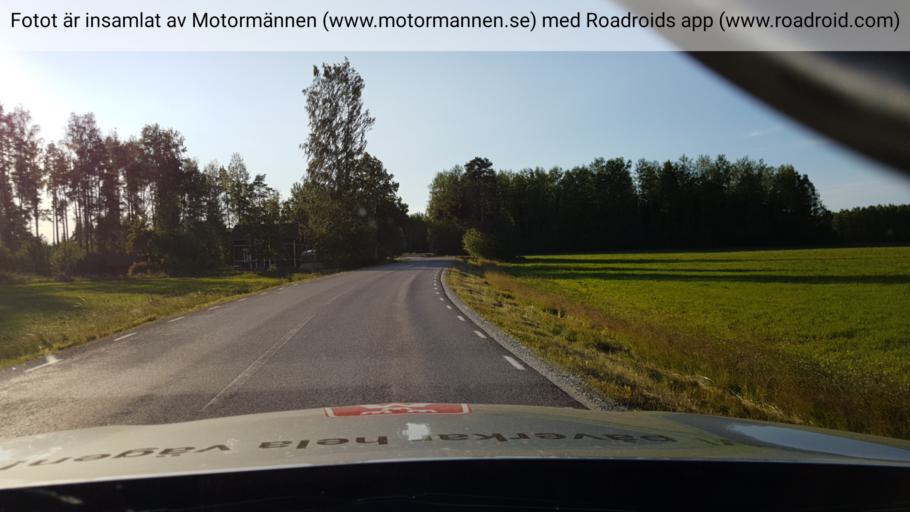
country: SE
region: Vaestmanland
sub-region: Surahammars Kommun
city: Ramnas
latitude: 59.9208
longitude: 16.3143
